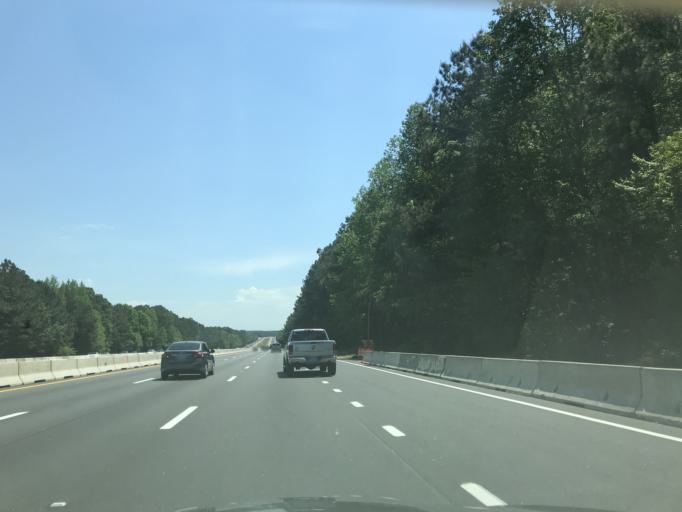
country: US
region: North Carolina
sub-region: Wake County
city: Garner
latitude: 35.7455
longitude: -78.5931
